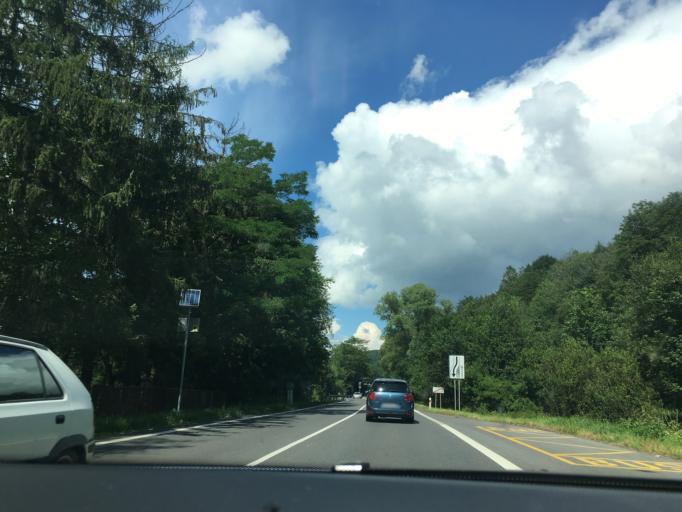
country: SK
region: Presovsky
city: Svidnik
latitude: 49.3652
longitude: 21.6887
